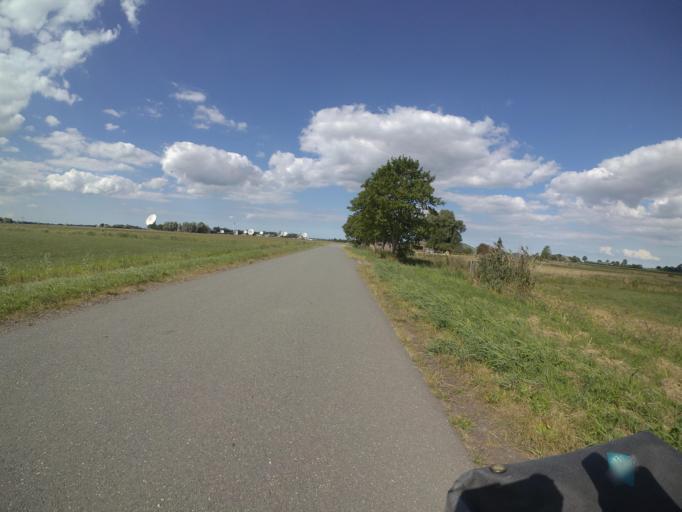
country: NL
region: Friesland
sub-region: Gemeente Kollumerland en Nieuwkruisland
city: Kollum
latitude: 53.2778
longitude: 6.2229
